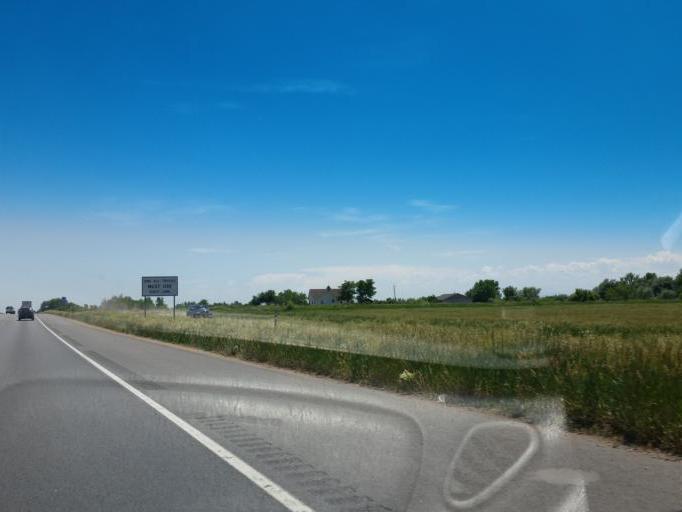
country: US
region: Colorado
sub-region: Larimer County
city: Fort Collins
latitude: 40.5502
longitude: -104.9992
